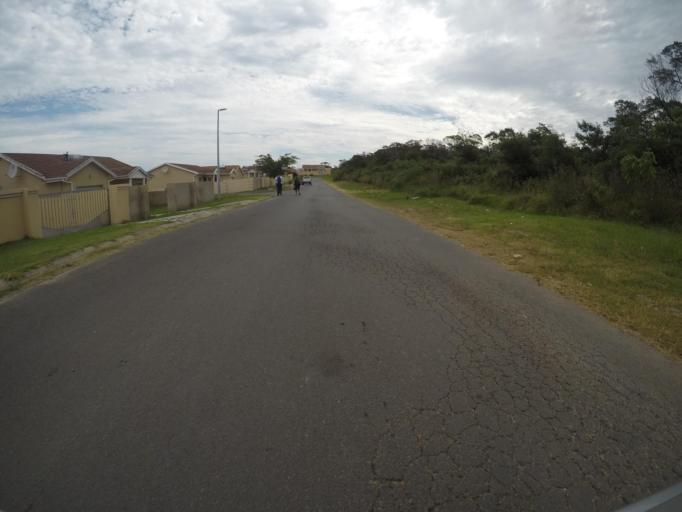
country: ZA
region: Eastern Cape
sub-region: Buffalo City Metropolitan Municipality
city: East London
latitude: -32.9901
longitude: 27.8442
